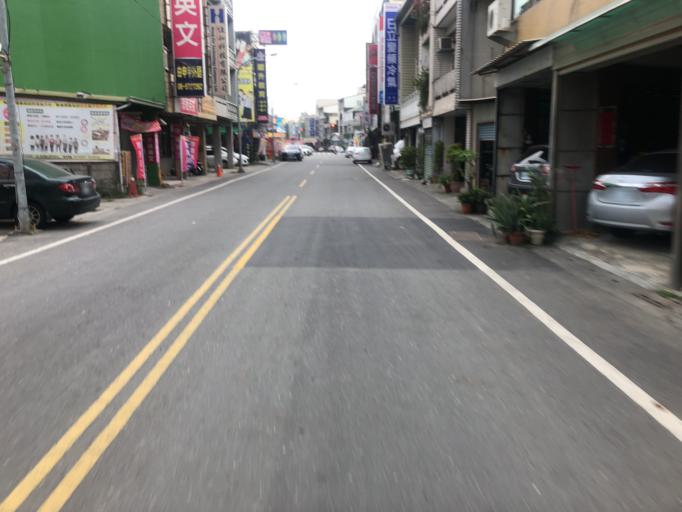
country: TW
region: Taiwan
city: Xinying
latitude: 23.1849
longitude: 120.2532
